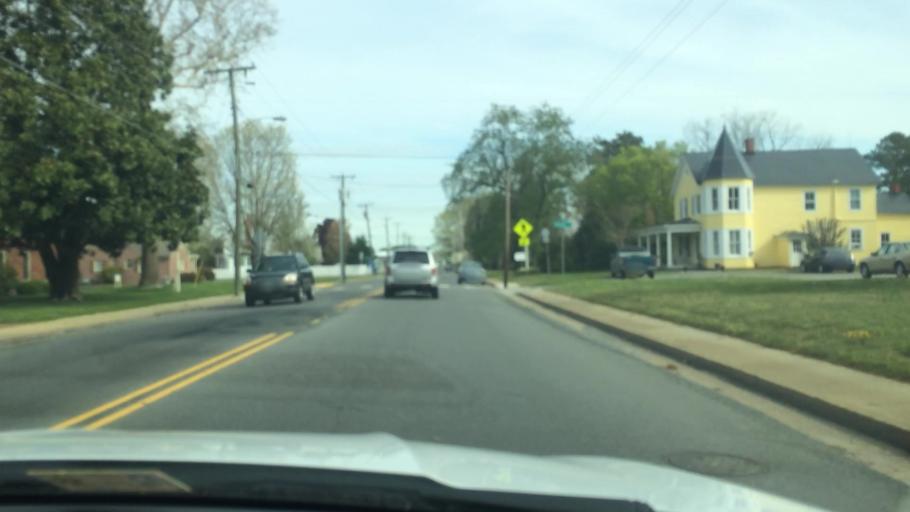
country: US
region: Virginia
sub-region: Lancaster County
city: Kilmarnock
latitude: 37.7064
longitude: -76.3788
